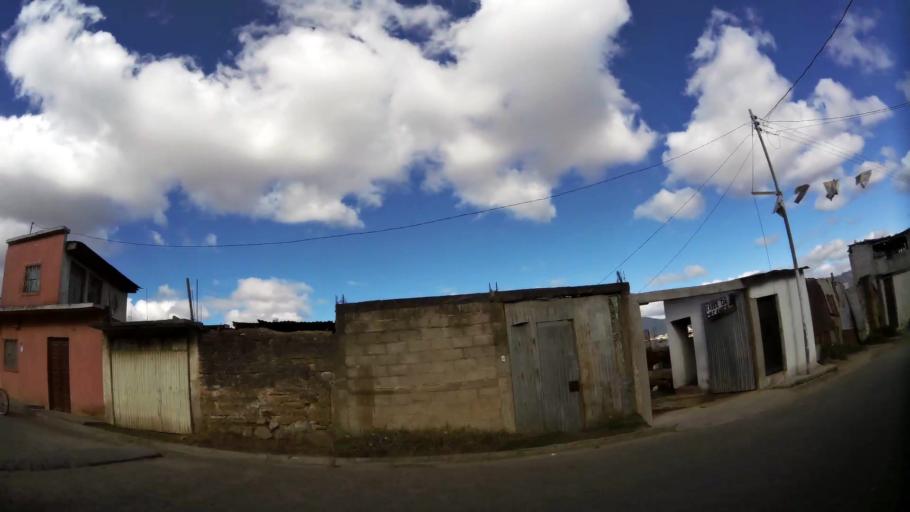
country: GT
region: Quetzaltenango
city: Quetzaltenango
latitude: 14.8317
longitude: -91.5095
